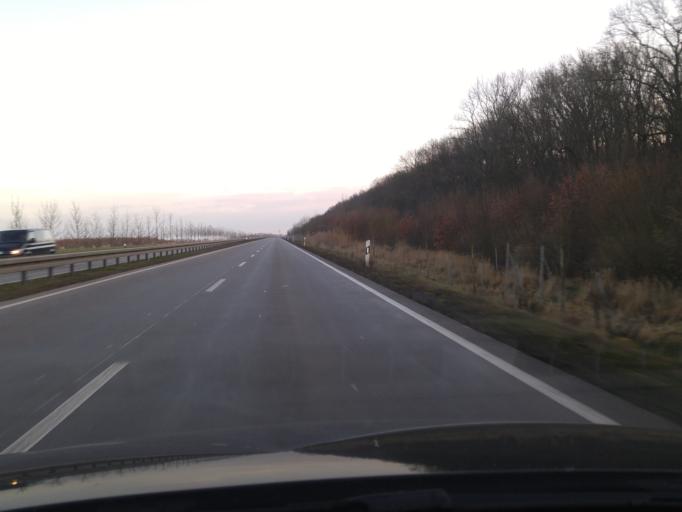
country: DE
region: Saxony
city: Rackwitz
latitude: 51.4102
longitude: 12.3186
